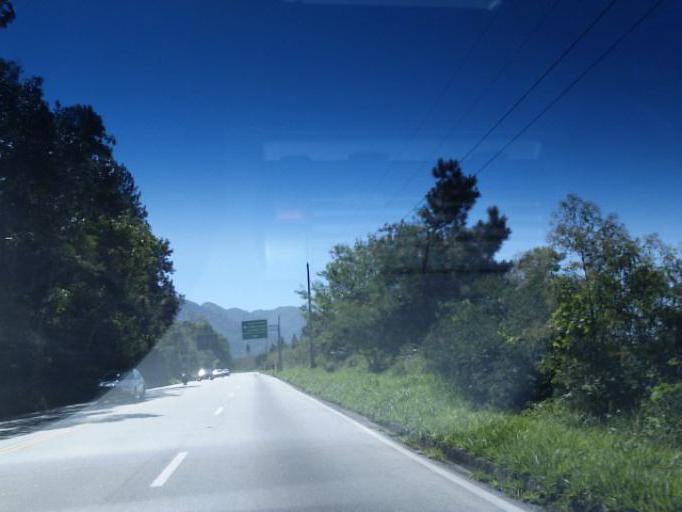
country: BR
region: Sao Paulo
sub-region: Campos Do Jordao
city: Campos do Jordao
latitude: -22.8405
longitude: -45.6219
